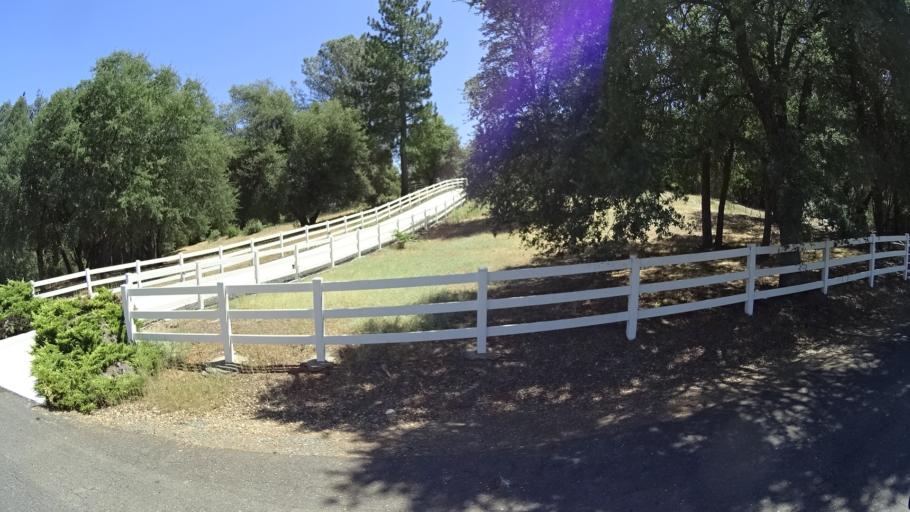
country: US
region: California
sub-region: Calaveras County
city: Murphys
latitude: 38.1291
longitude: -120.4502
